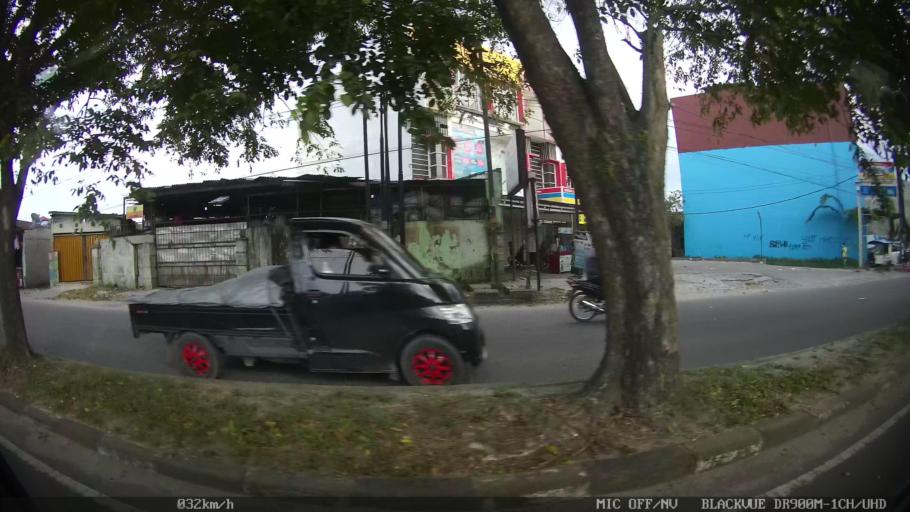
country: ID
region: North Sumatra
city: Sunggal
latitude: 3.5526
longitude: 98.6114
